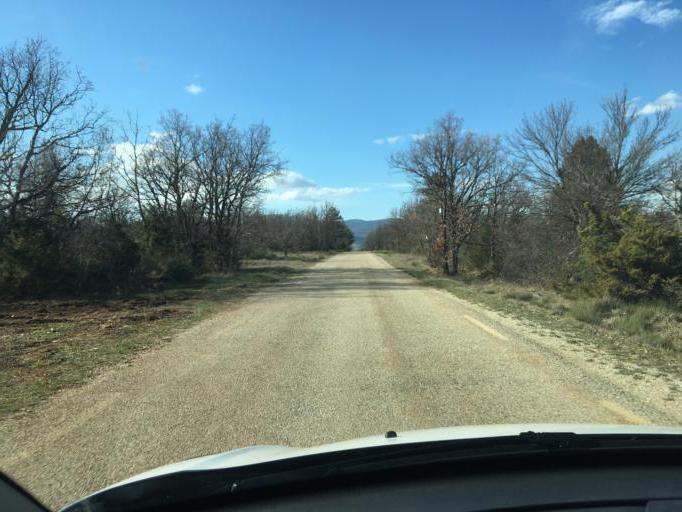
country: FR
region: Provence-Alpes-Cote d'Azur
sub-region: Departement du Vaucluse
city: Sault
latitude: 44.0683
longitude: 5.4274
